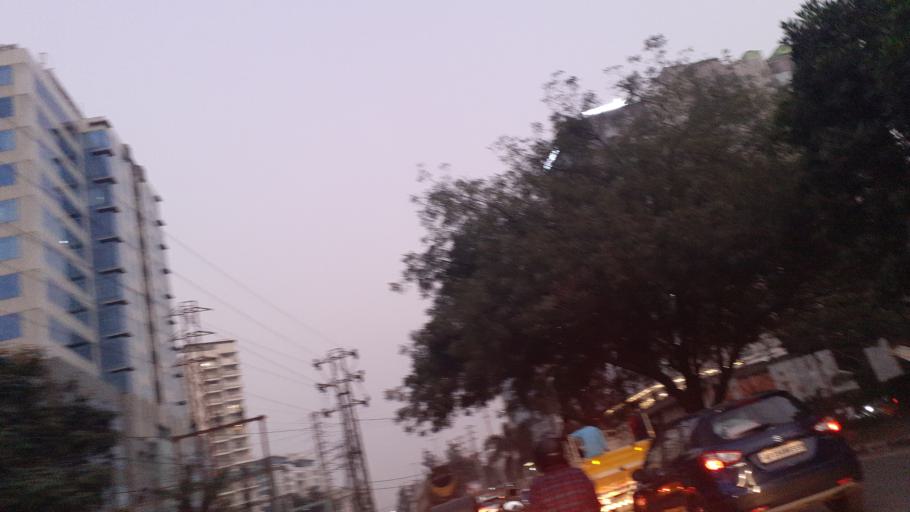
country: IN
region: Telangana
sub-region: Rangareddi
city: Kukatpalli
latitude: 17.4588
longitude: 78.3673
